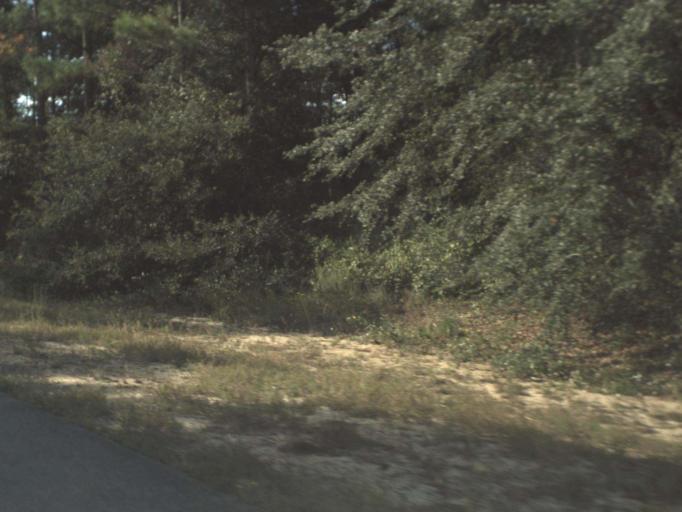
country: US
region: Florida
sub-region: Bay County
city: Laguna Beach
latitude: 30.4426
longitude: -85.8230
